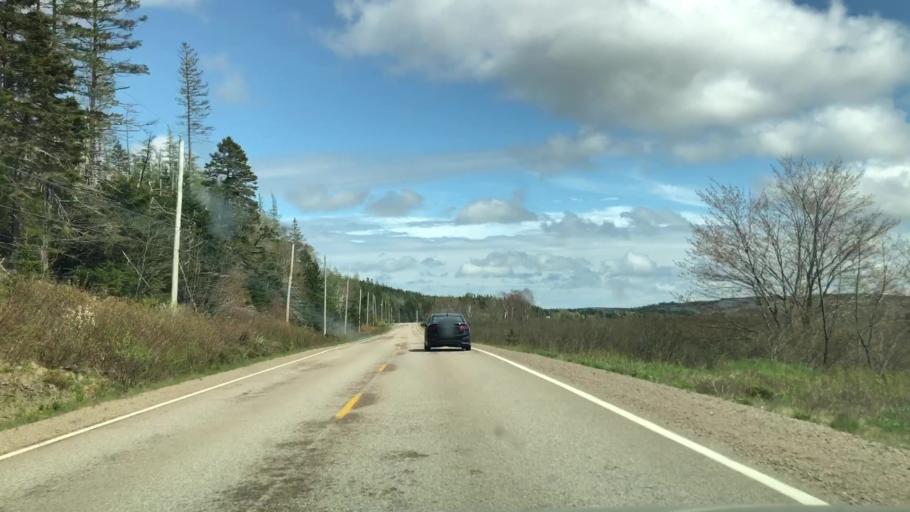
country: CA
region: Nova Scotia
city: Antigonish
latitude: 45.1935
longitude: -61.9964
